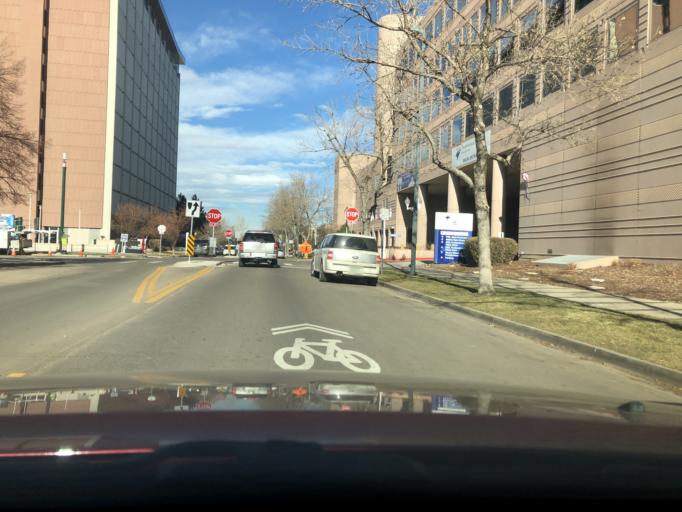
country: US
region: Colorado
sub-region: Denver County
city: Denver
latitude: 39.7467
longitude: -104.9684
